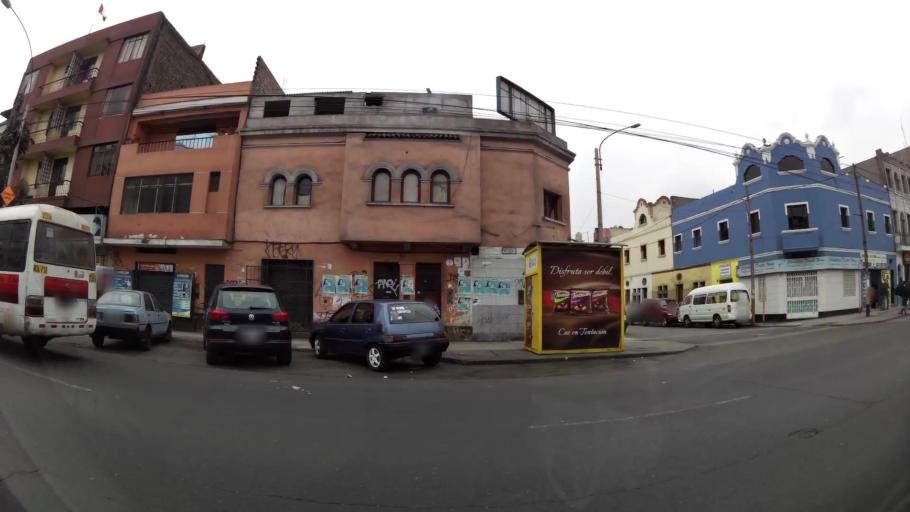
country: PE
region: Lima
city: Lima
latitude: -12.0554
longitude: -77.0533
